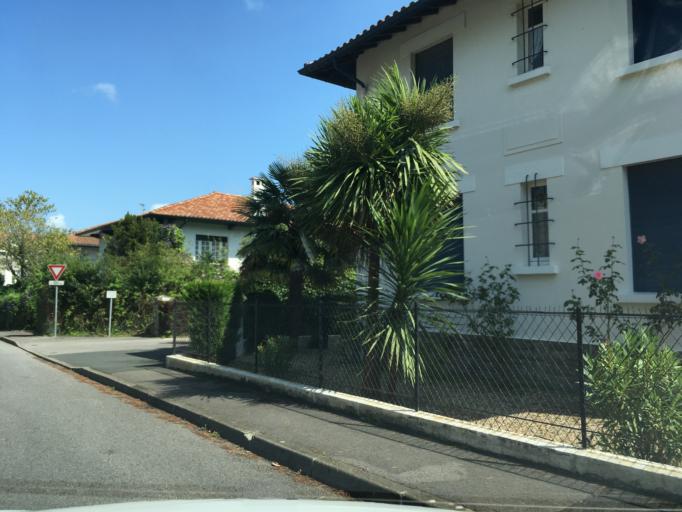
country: FR
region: Aquitaine
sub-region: Departement des Pyrenees-Atlantiques
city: Bayonne
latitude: 43.4916
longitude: -1.4883
